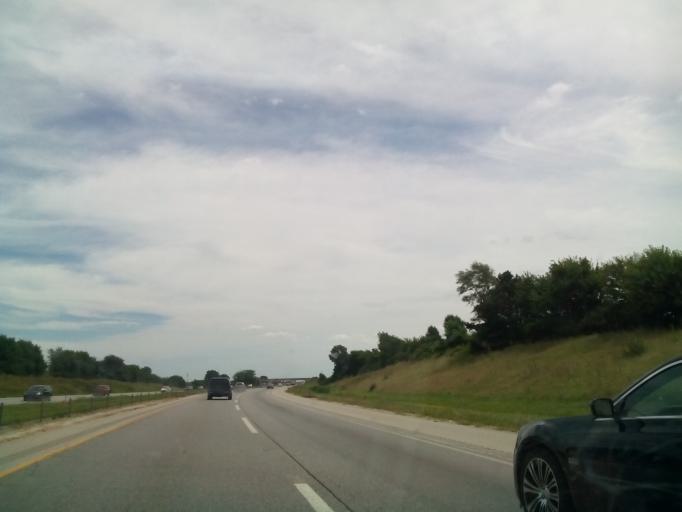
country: US
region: Illinois
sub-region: Kane County
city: Maple Park
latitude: 41.8991
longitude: -88.6458
